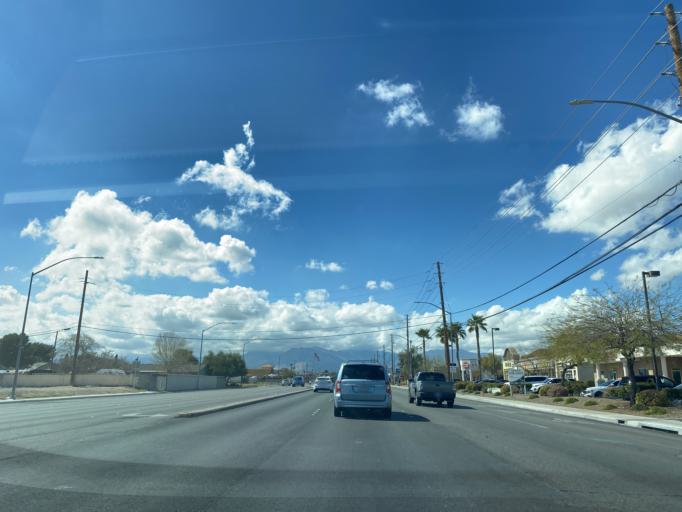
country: US
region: Nevada
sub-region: Clark County
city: Las Vegas
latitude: 36.2390
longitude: -115.2028
